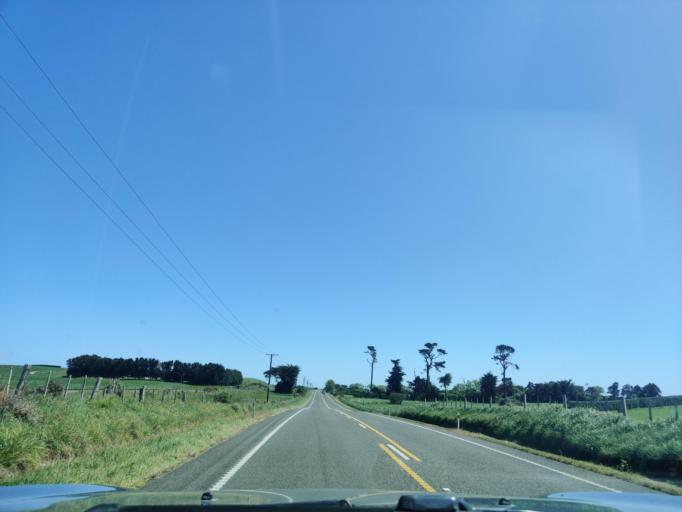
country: NZ
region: Taranaki
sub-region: South Taranaki District
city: Patea
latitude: -39.7759
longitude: 174.6818
